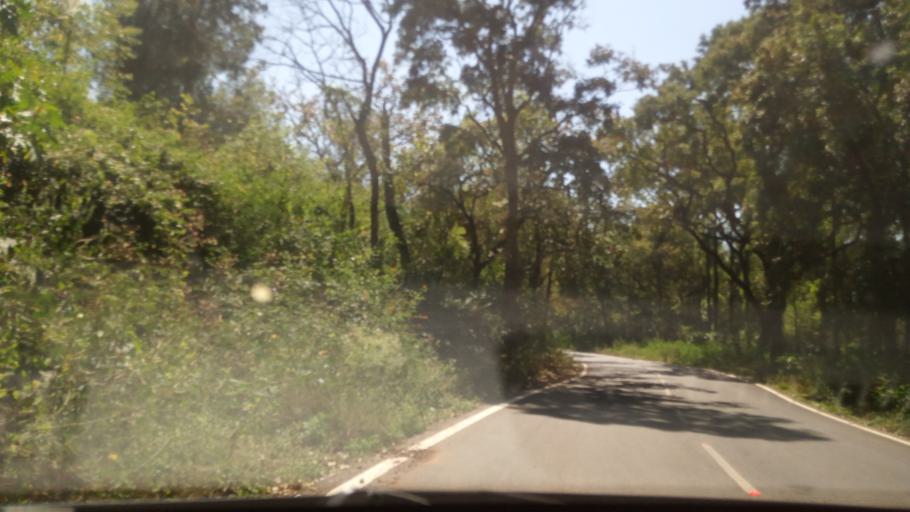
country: IN
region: Karnataka
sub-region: Chikmagalur
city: Chikmagalur
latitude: 13.4516
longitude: 75.8007
